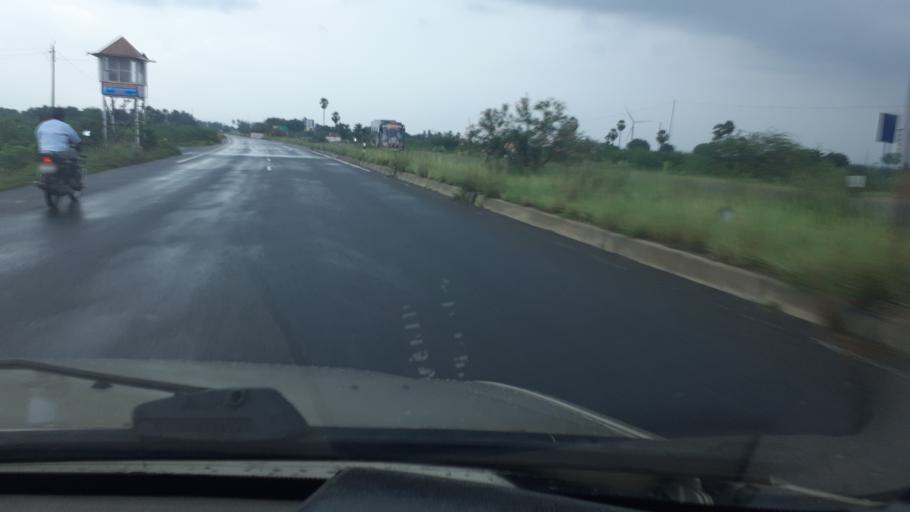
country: IN
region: Tamil Nadu
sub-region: Thoothukkudi
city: Kadambur
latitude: 9.0411
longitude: 77.7916
